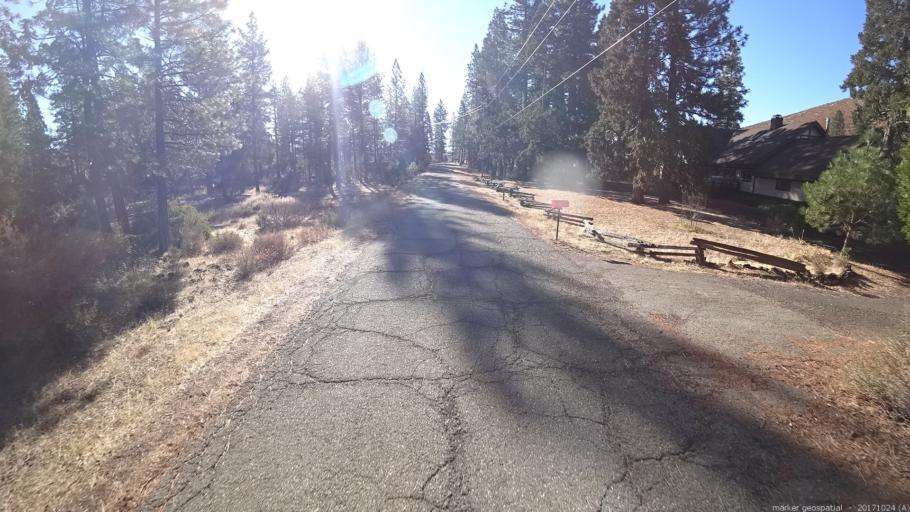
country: US
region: California
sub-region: Shasta County
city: Burney
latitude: 40.8383
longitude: -121.5146
